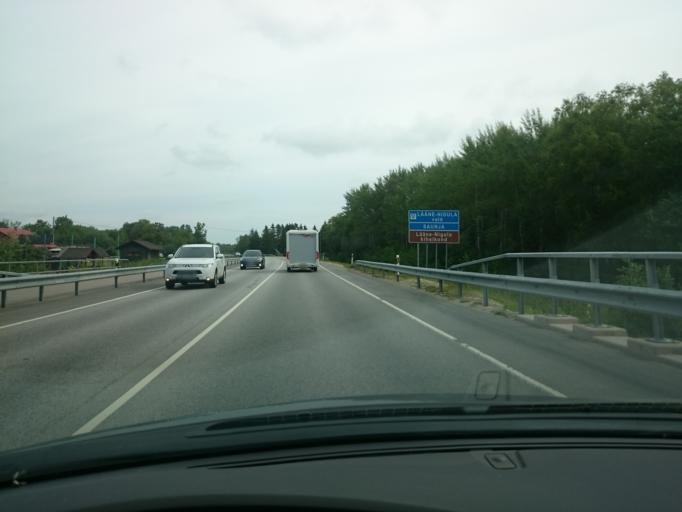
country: EE
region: Laeaene
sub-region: Ridala Parish
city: Uuemoisa
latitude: 58.9510
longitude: 23.6562
